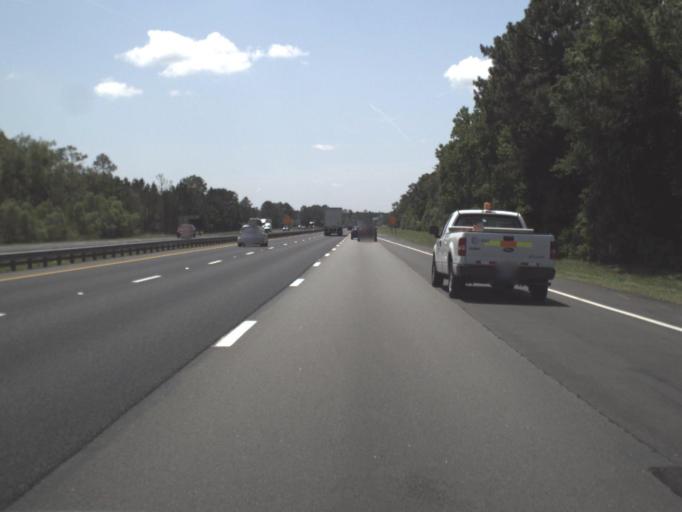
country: US
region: Florida
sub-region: Nassau County
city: Yulee
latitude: 30.6139
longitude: -81.6482
